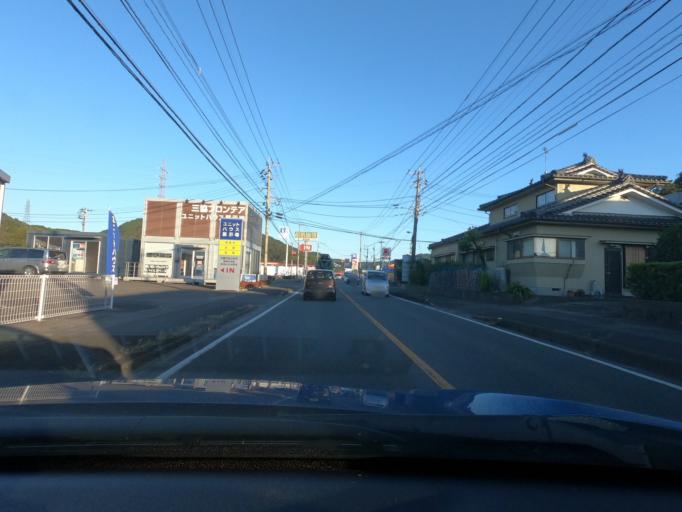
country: JP
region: Kagoshima
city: Satsumasendai
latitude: 31.8091
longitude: 130.3346
